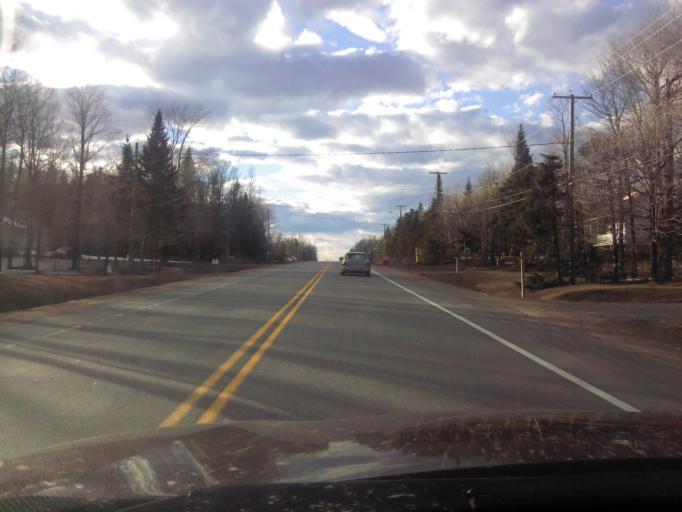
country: CA
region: Quebec
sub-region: Capitale-Nationale
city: Sainte Catherine de la Jacques Cartier
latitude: 46.8004
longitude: -71.5532
